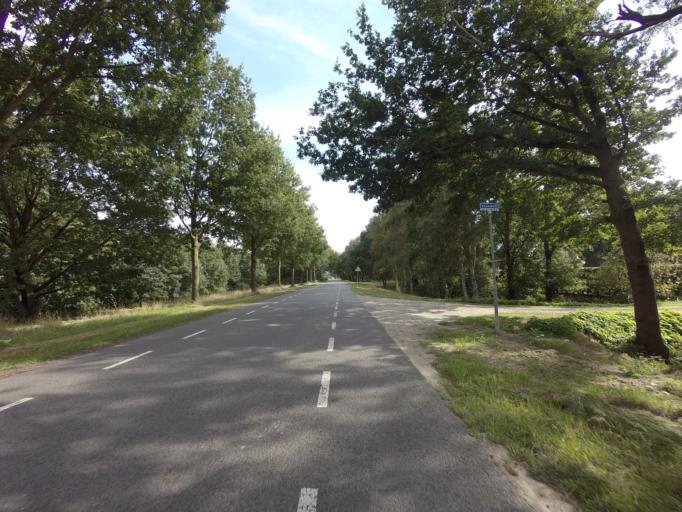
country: NL
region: Drenthe
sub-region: Gemeente Coevorden
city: Coevorden
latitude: 52.6798
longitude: 6.7159
